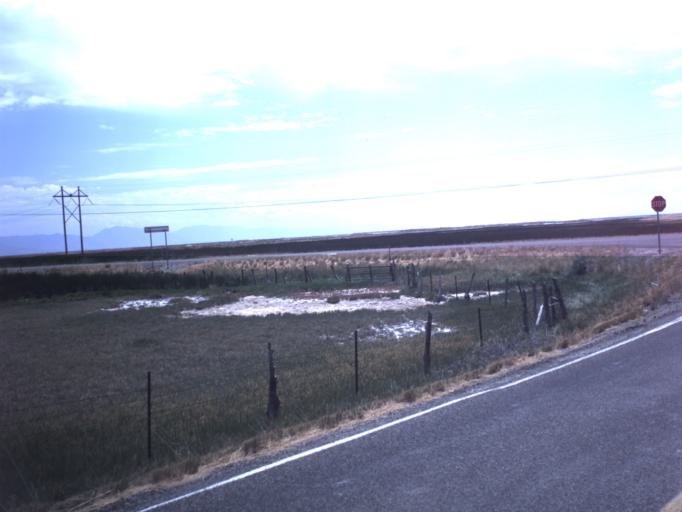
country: US
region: Utah
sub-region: Box Elder County
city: Tremonton
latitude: 41.6133
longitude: -112.3671
